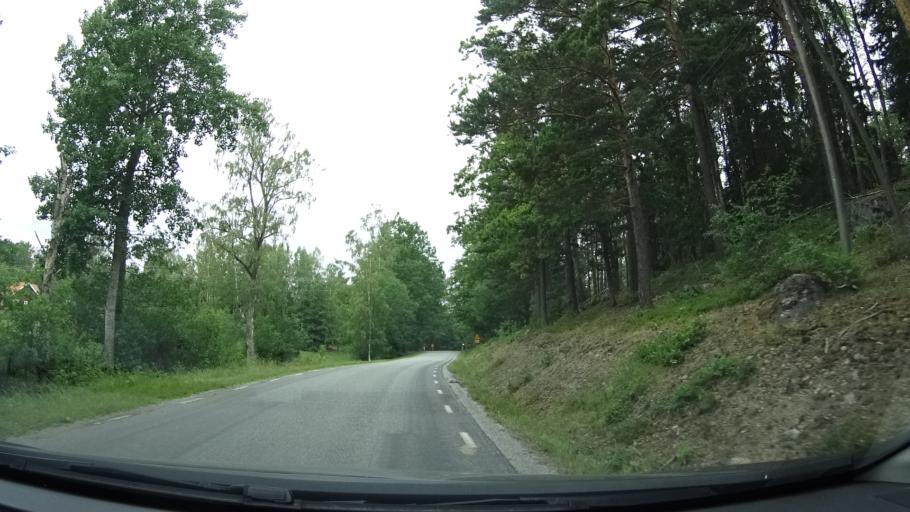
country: SE
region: Stockholm
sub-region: Varmdo Kommun
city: Mortnas
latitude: 59.3671
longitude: 18.4660
